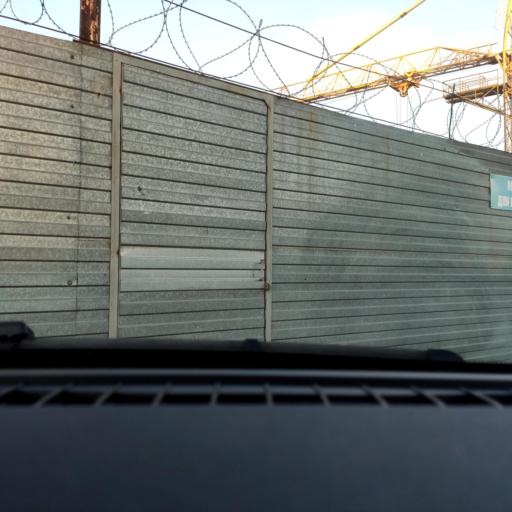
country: RU
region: Voronezj
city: Maslovka
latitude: 51.6402
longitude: 39.2856
